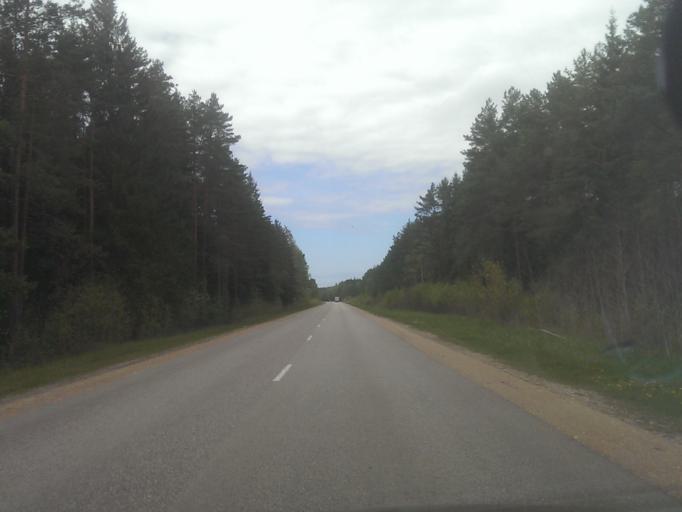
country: LV
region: Ventspils Rajons
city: Piltene
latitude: 57.1515
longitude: 21.7038
